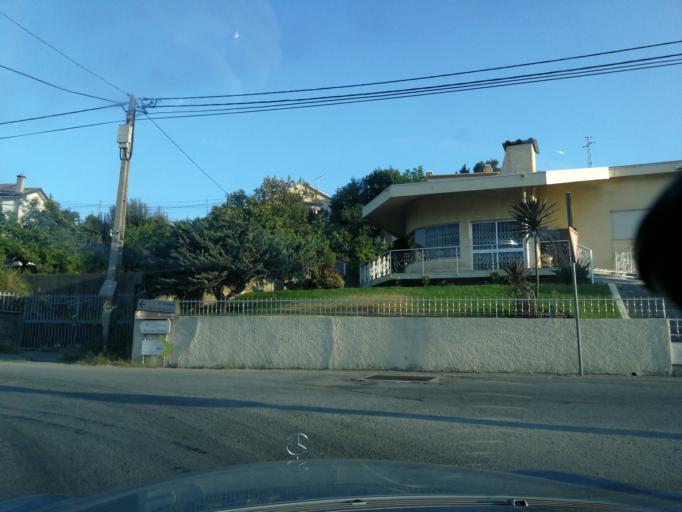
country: PT
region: Braga
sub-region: Braga
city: Braga
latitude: 41.5316
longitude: -8.4277
